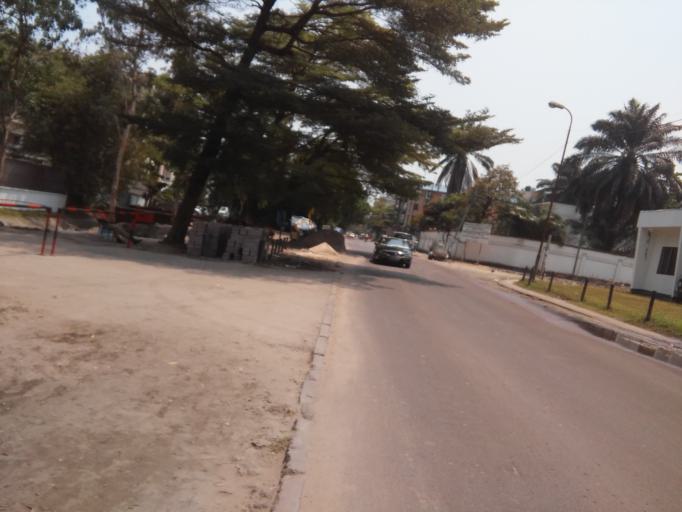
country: CD
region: Kinshasa
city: Kinshasa
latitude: -4.3186
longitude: 15.2844
